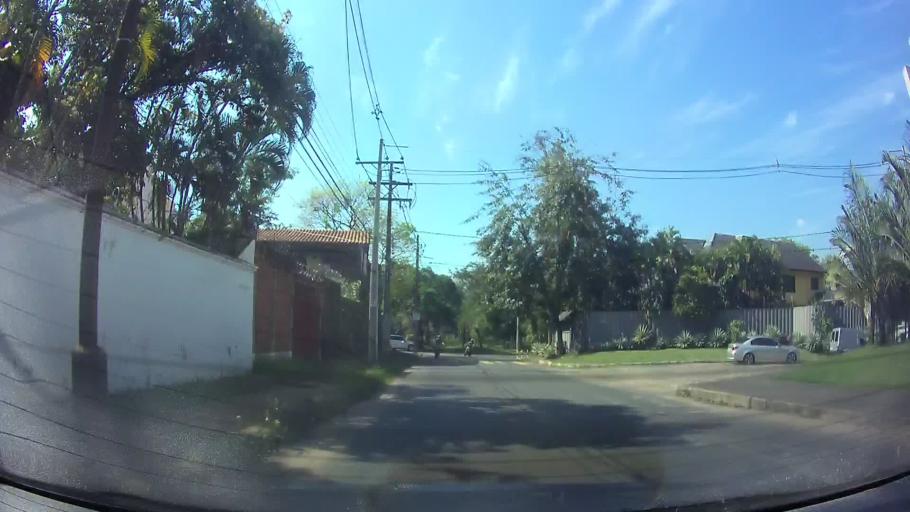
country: PY
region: Central
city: Fernando de la Mora
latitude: -25.2854
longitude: -57.5544
